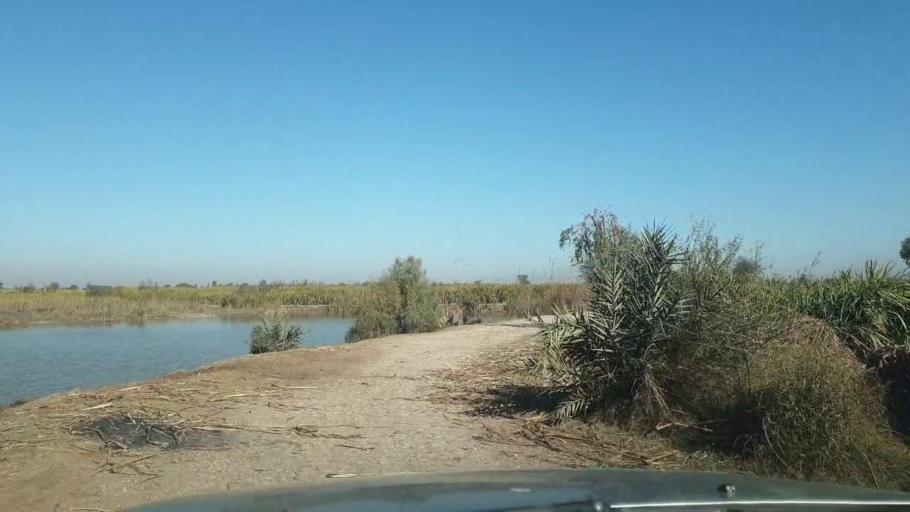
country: PK
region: Sindh
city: Ghotki
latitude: 28.0201
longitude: 69.2830
